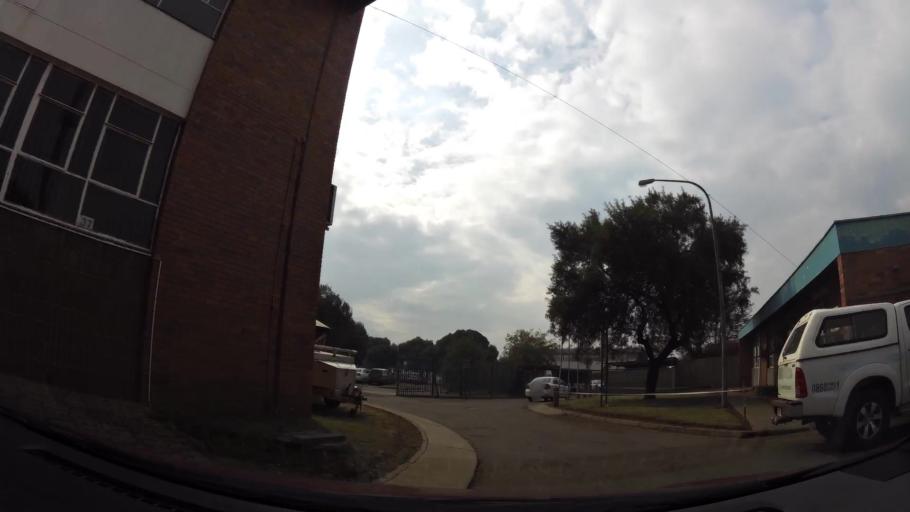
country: ZA
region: Gauteng
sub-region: Sedibeng District Municipality
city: Vanderbijlpark
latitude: -26.6823
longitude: 27.8353
